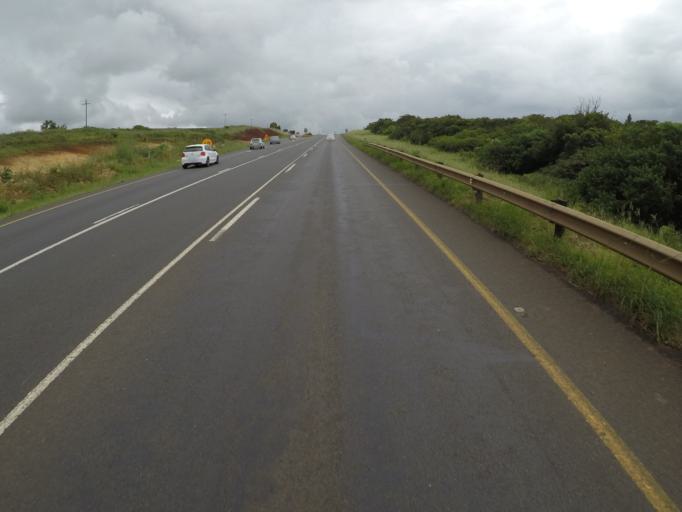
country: ZA
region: KwaZulu-Natal
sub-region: uThungulu District Municipality
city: Empangeni
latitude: -28.7766
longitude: 31.9282
